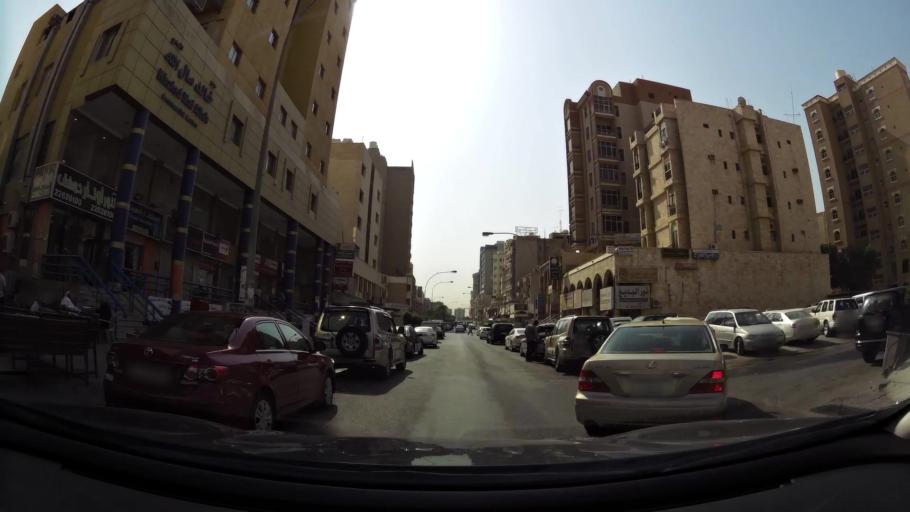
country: KW
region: Muhafazat Hawalli
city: Hawalli
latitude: 29.3311
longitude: 48.0187
